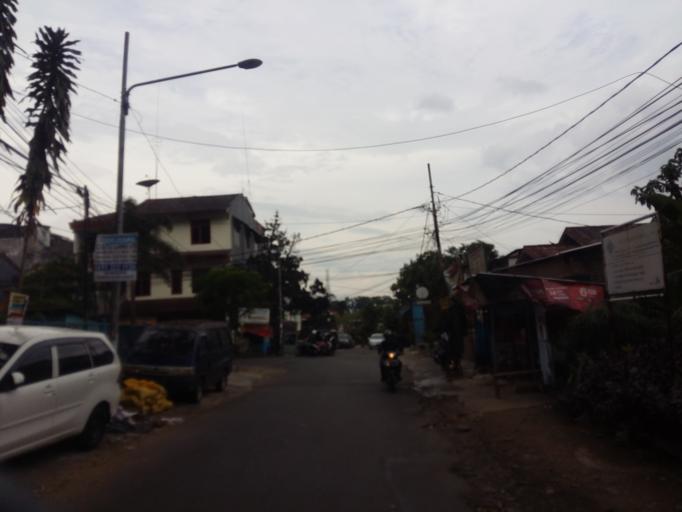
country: ID
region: West Java
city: Bandung
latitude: -6.8829
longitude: 107.6113
